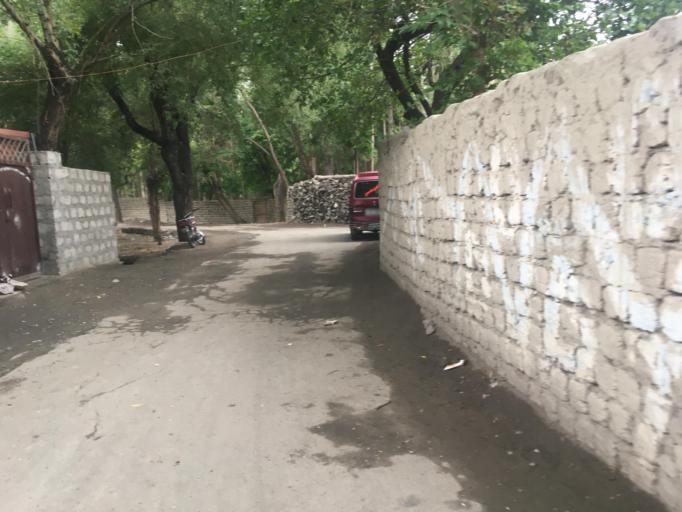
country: PK
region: Gilgit-Baltistan
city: Skardu
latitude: 35.2917
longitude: 75.6506
